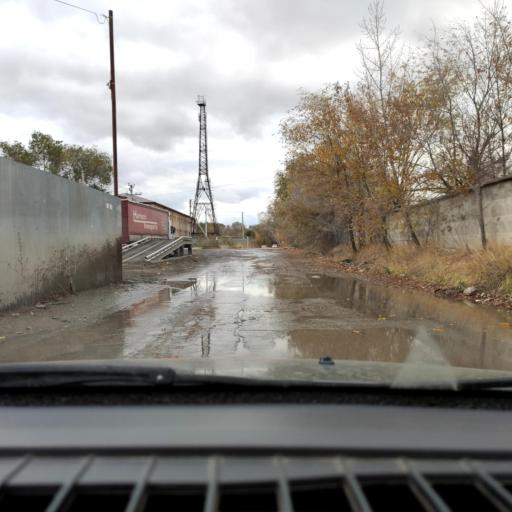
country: RU
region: Samara
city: Tol'yatti
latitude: 53.5714
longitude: 49.2827
